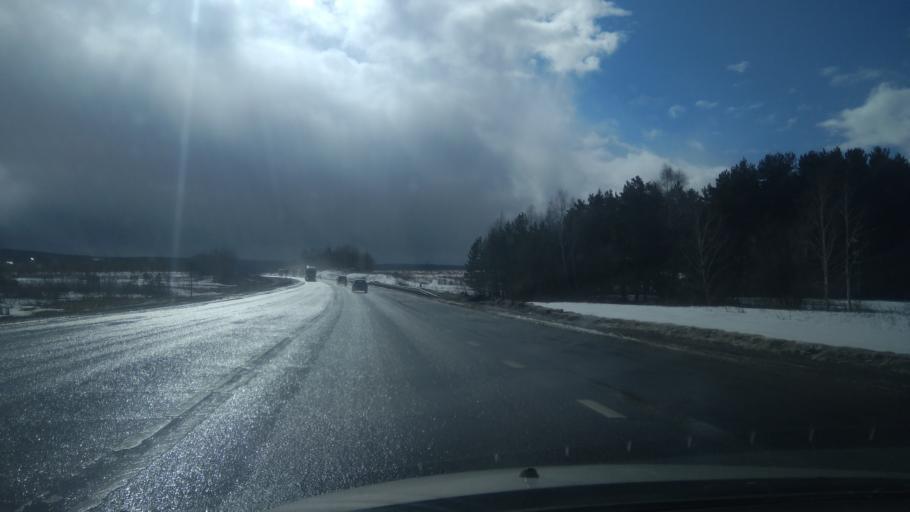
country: RU
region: Perm
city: Kungur
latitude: 57.3821
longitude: 56.9057
